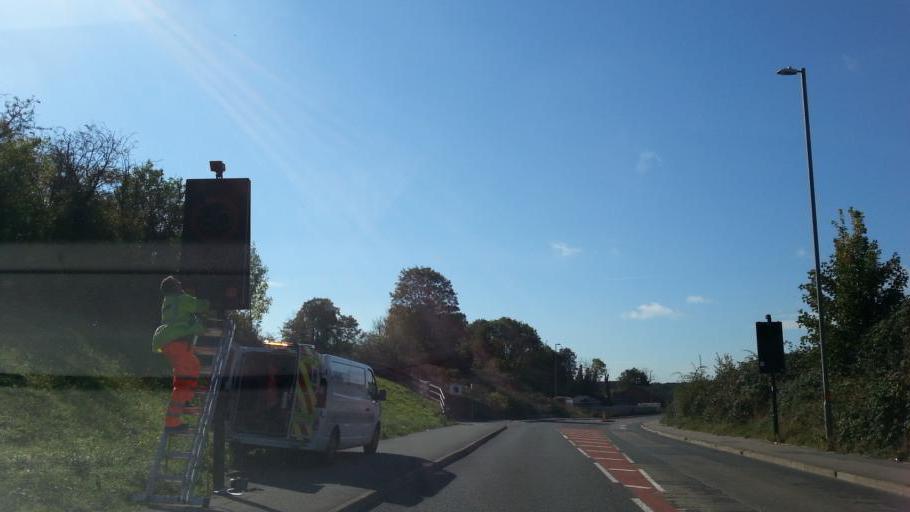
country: GB
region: England
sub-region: Northamptonshire
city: Higham Ferrers
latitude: 52.2962
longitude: -0.5938
